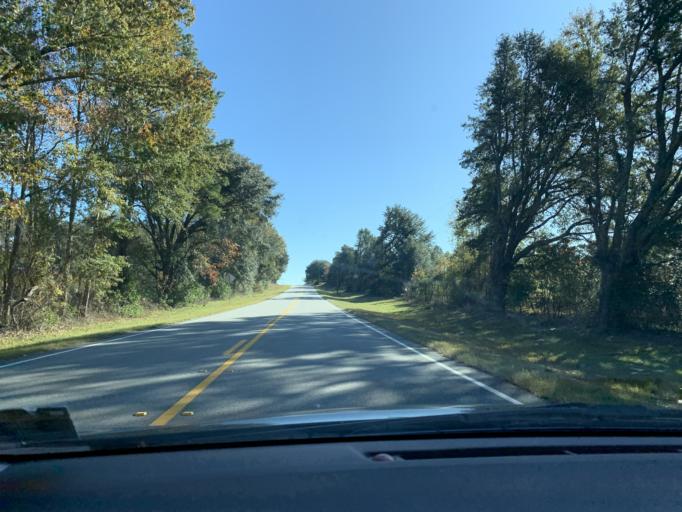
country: US
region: Georgia
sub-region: Ben Hill County
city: Fitzgerald
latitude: 31.7776
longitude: -83.0756
